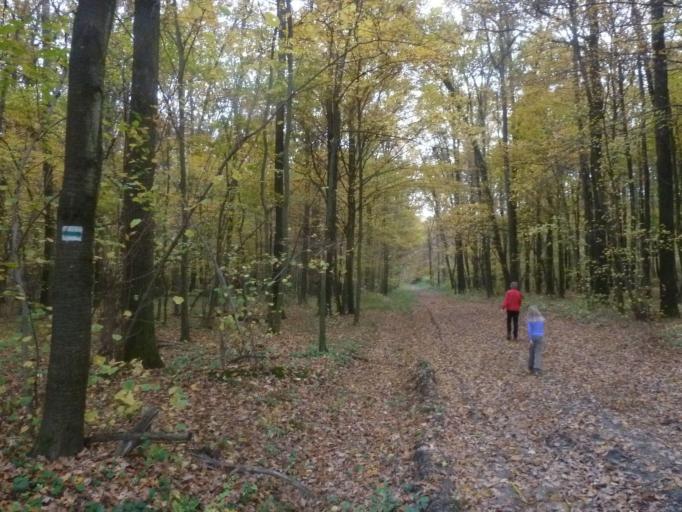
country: HU
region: Zala
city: Nagykanizsa
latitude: 46.5278
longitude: 17.0228
